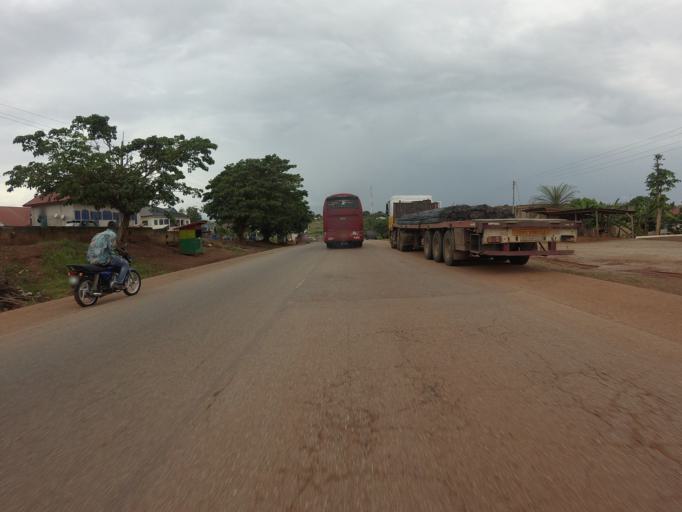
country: GH
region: Ashanti
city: Konongo
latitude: 6.6174
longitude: -1.1836
